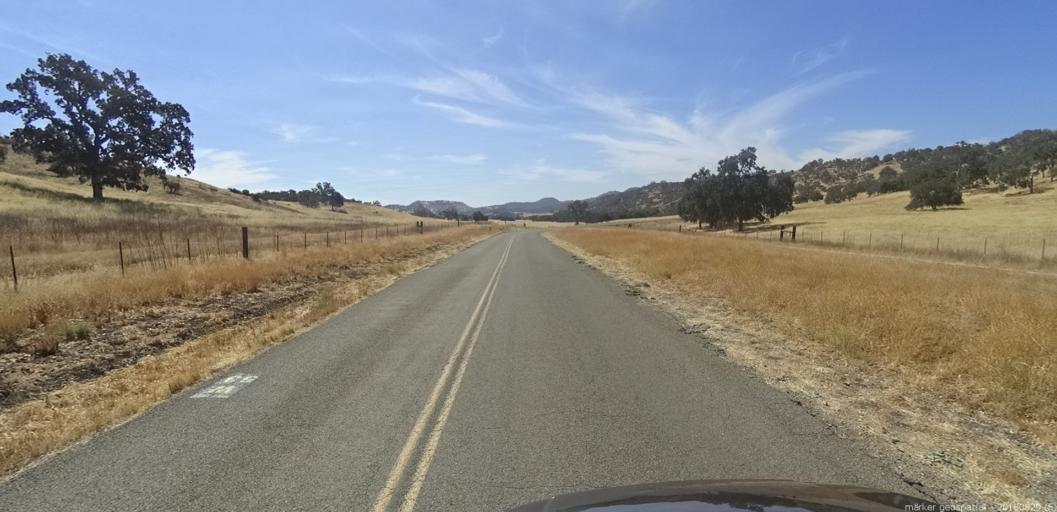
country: US
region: California
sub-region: San Luis Obispo County
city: Lake Nacimiento
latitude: 35.8308
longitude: -120.9762
